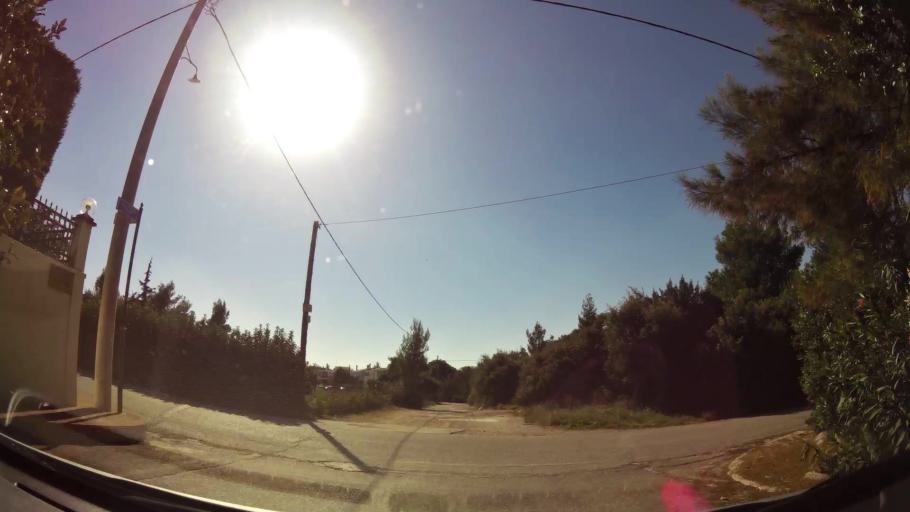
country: GR
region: Attica
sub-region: Nomarchia Athinas
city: Nea Erythraia
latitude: 38.1031
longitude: 23.8265
